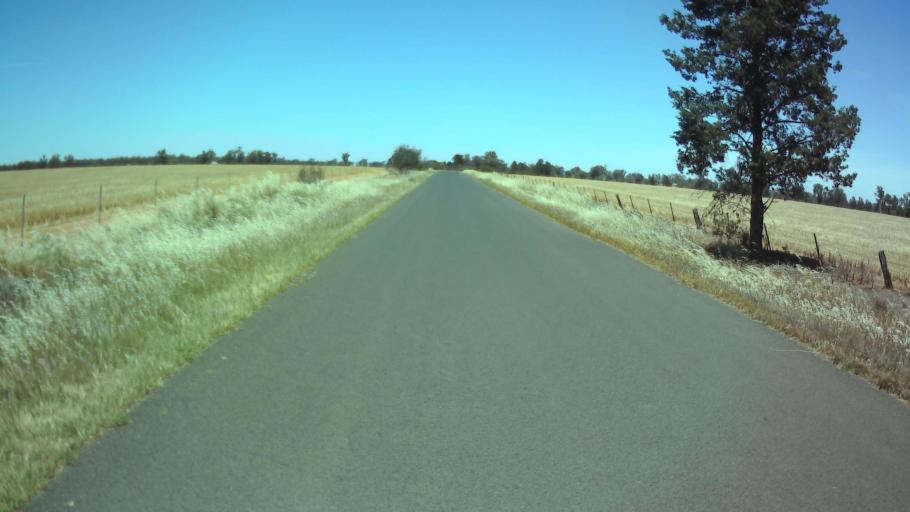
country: AU
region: New South Wales
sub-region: Weddin
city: Grenfell
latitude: -34.0529
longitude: 147.7813
